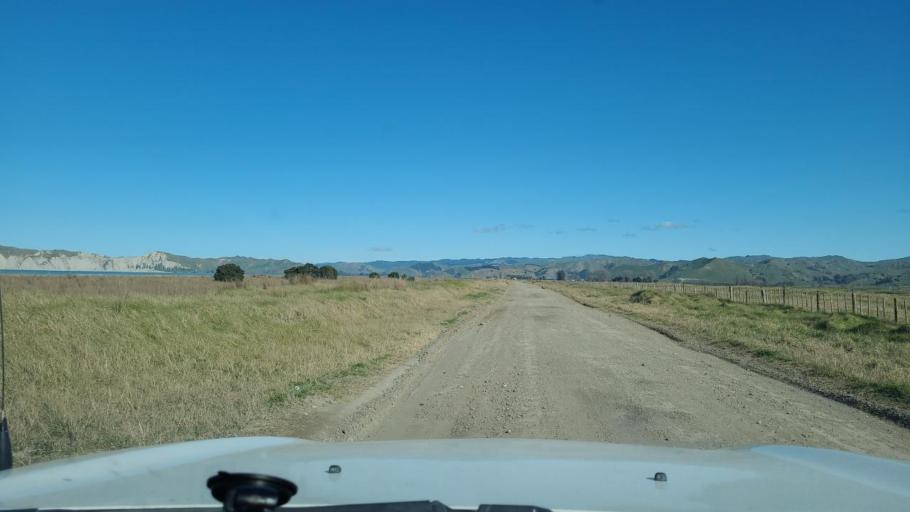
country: NZ
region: Gisborne
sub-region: Gisborne District
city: Gisborne
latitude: -38.7037
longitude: 177.9467
